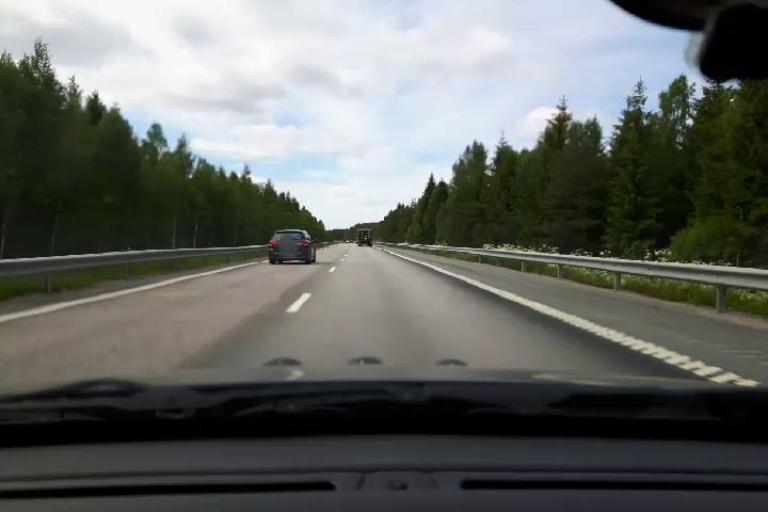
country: SE
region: Uppsala
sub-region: Alvkarleby Kommun
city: AElvkarleby
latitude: 60.4890
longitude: 17.3481
